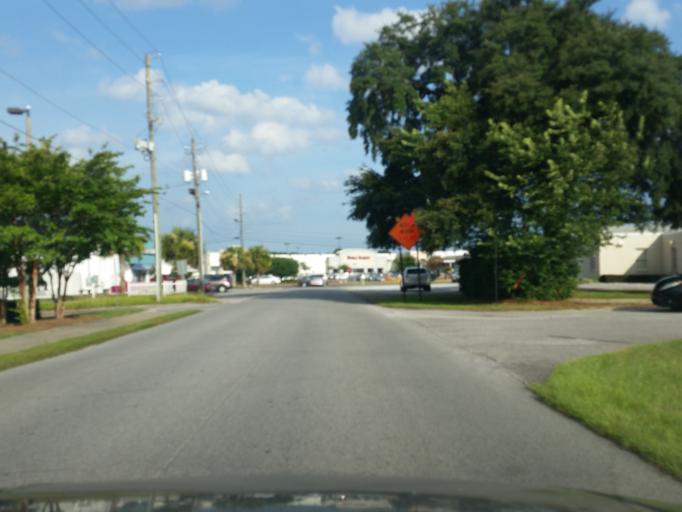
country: US
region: Florida
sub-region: Escambia County
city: Brent
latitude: 30.4787
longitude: -87.2098
